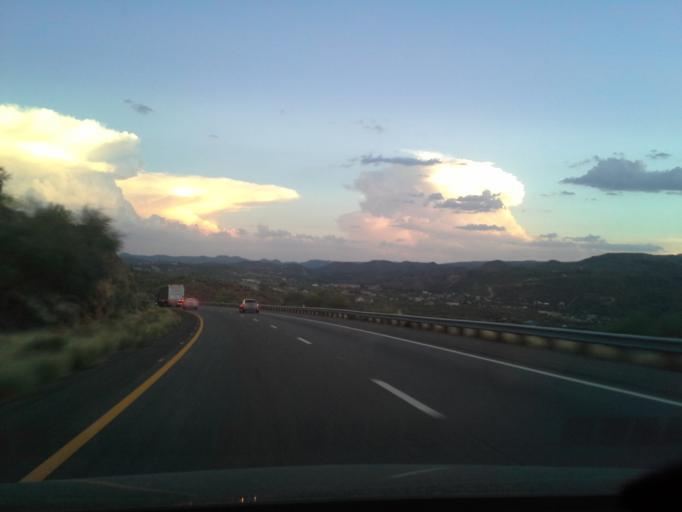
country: US
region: Arizona
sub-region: Yavapai County
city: Black Canyon City
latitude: 34.1085
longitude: -112.1443
